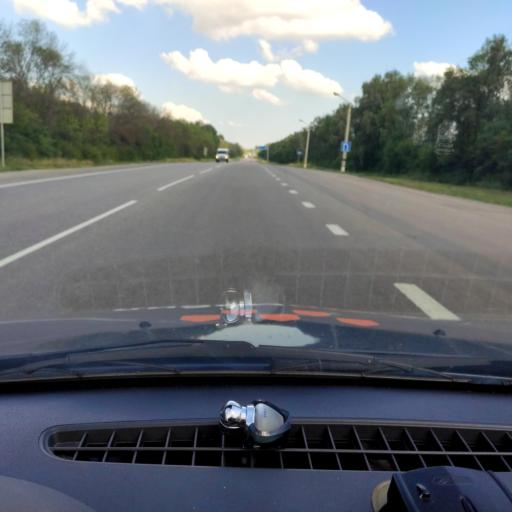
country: RU
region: Lipetsk
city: Yelets
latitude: 52.5876
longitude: 38.6100
